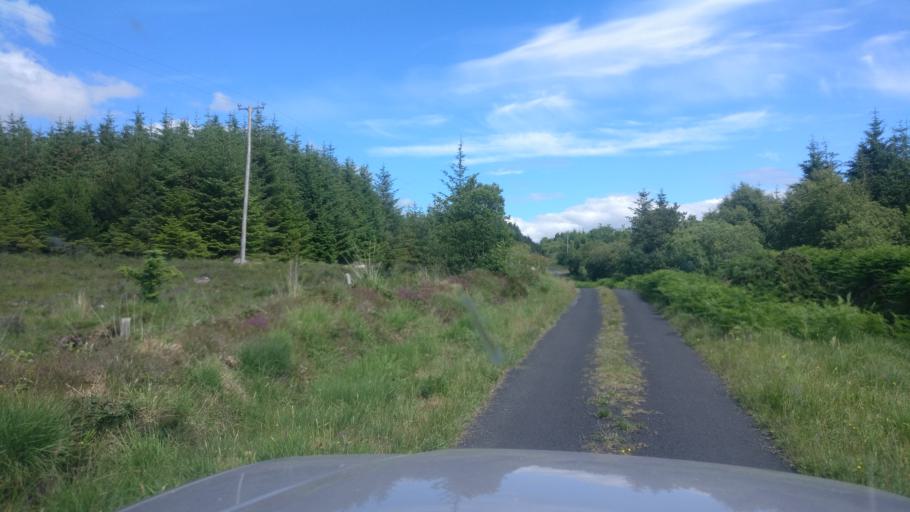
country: IE
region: Connaught
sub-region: County Galway
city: Gort
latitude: 53.0640
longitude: -8.6953
